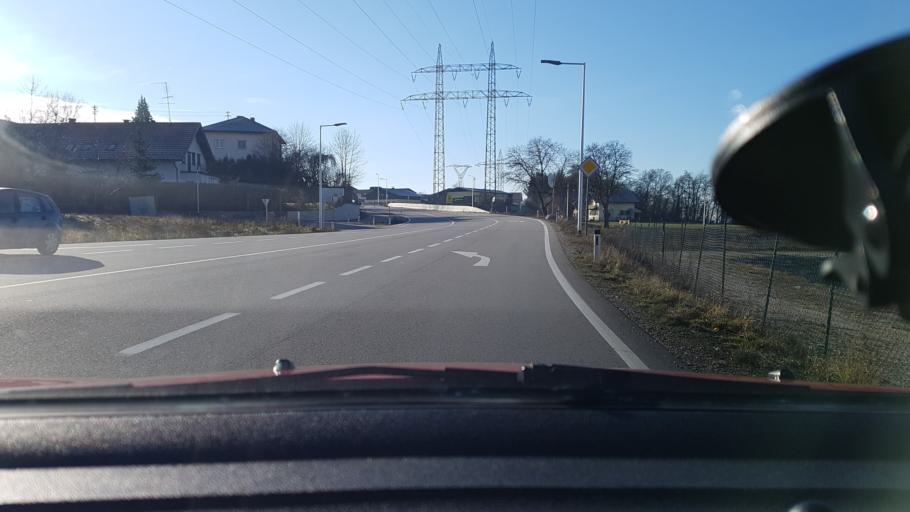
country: AT
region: Upper Austria
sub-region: Politischer Bezirk Braunau am Inn
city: Braunau am Inn
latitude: 48.2398
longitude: 13.0362
